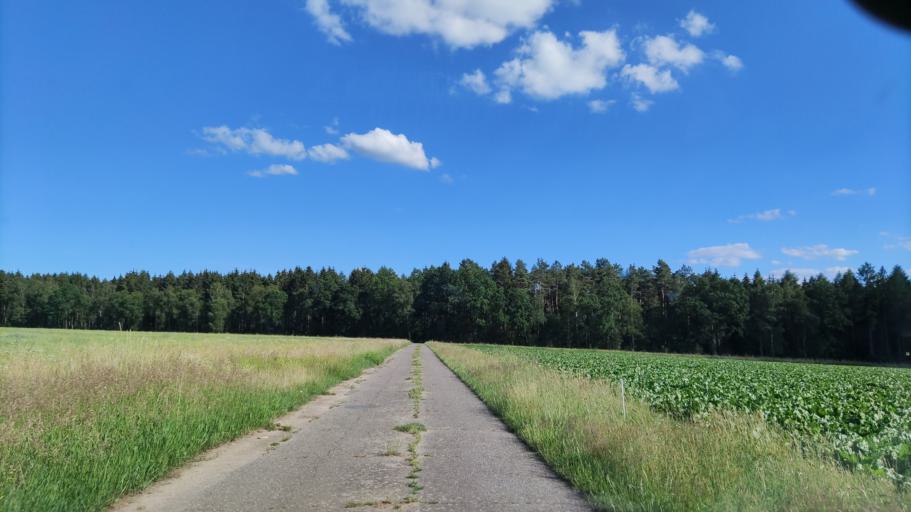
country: DE
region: Lower Saxony
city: Hanstedt Eins
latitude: 53.0839
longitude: 10.4080
